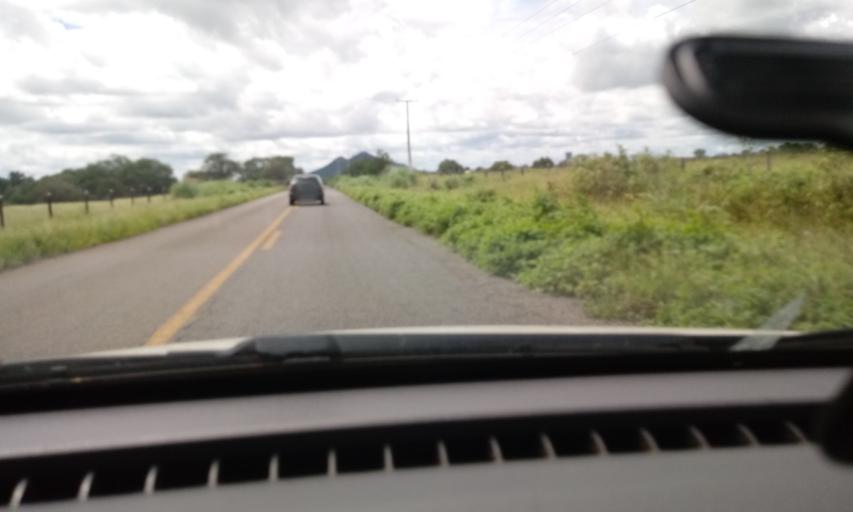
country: BR
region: Bahia
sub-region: Guanambi
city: Guanambi
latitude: -14.0994
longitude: -42.8714
